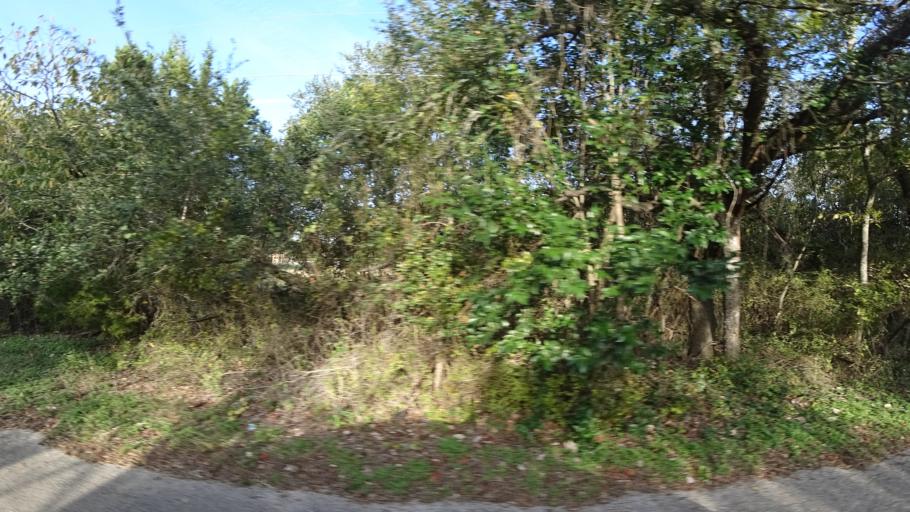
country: US
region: Texas
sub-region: Travis County
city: Barton Creek
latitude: 30.2472
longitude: -97.9206
